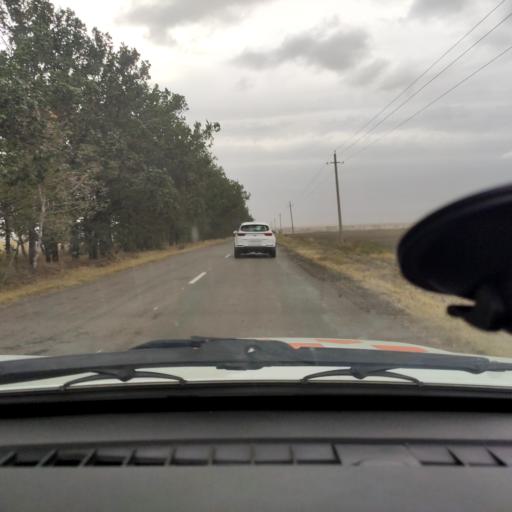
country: RU
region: Lipetsk
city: Khlevnoye
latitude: 52.0063
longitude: 39.1562
